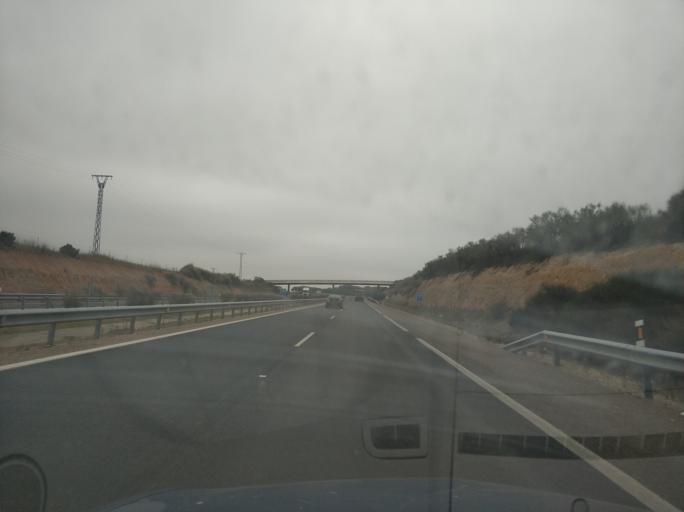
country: ES
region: Castille and Leon
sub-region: Provincia de Valladolid
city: Alaejos
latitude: 41.3118
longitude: -5.2238
